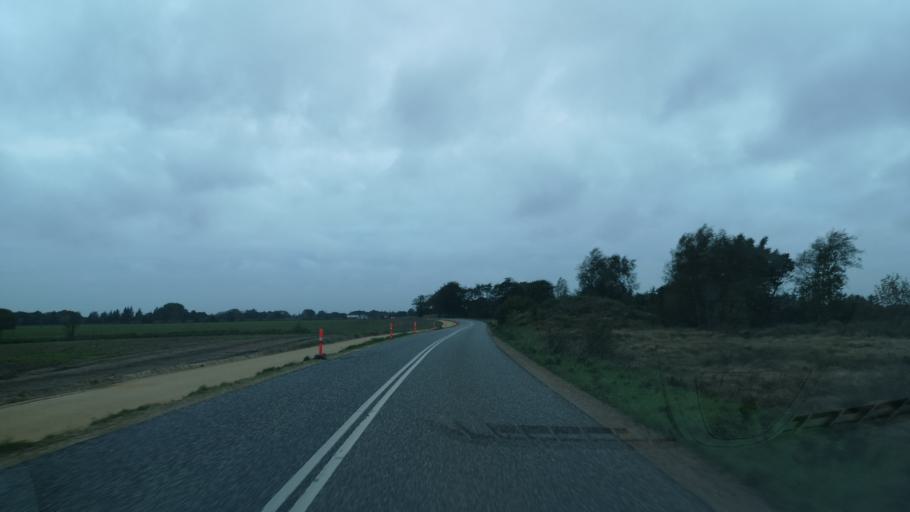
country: DK
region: Central Jutland
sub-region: Ringkobing-Skjern Kommune
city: Videbaek
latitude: 56.0543
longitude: 8.6377
